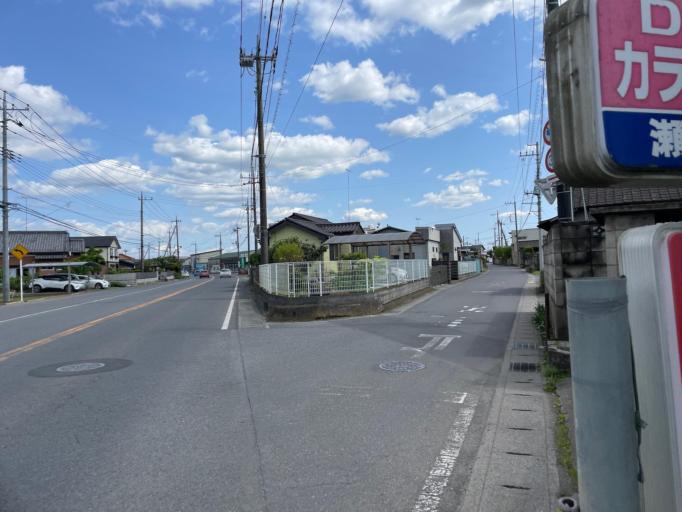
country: JP
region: Tochigi
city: Sano
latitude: 36.3201
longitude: 139.6425
